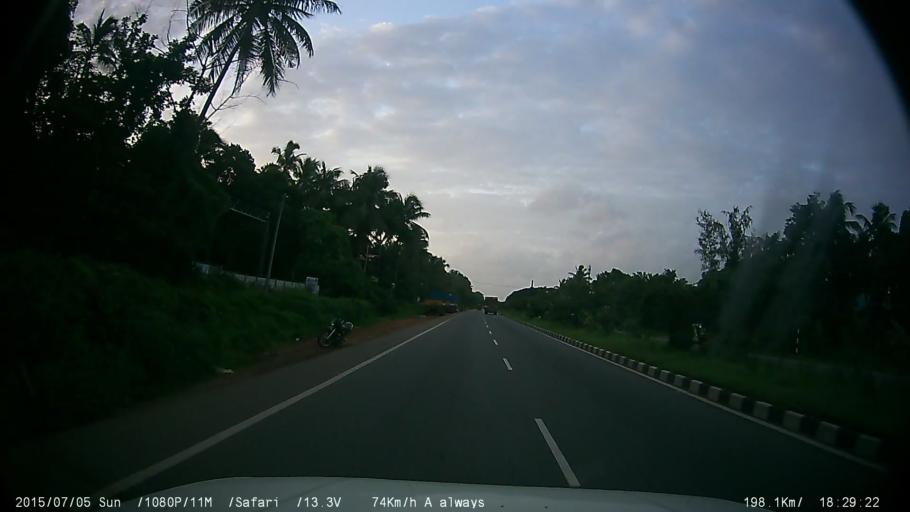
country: IN
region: Kerala
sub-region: Thrissur District
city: Trichur
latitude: 10.4712
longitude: 76.2576
